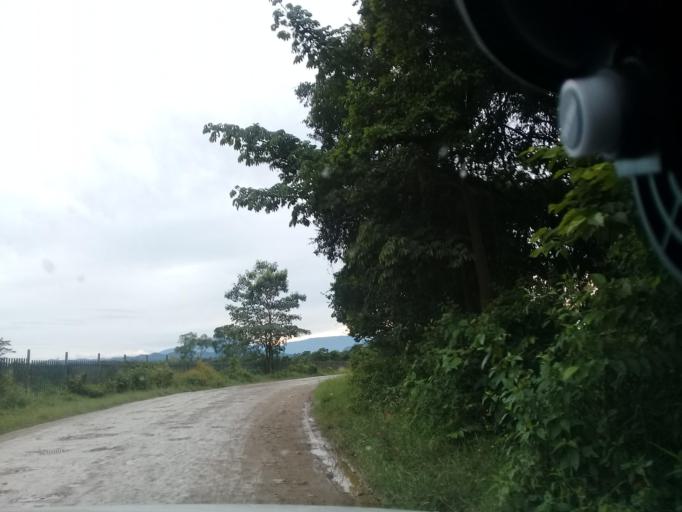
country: MX
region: Hidalgo
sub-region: Huejutla de Reyes
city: Chalahuiyapa
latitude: 21.1592
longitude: -98.3673
